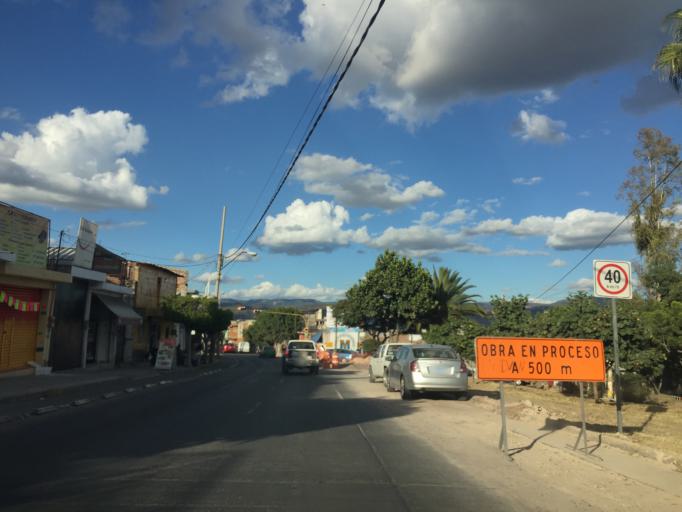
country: MX
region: Guanajuato
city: Leon
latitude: 21.1276
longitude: -101.7046
